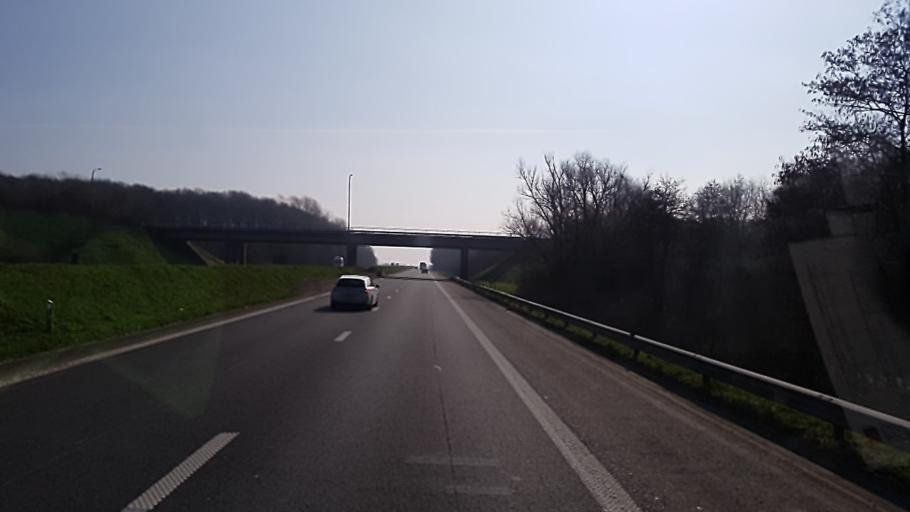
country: BE
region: Flanders
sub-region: Provincie West-Vlaanderen
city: Wervik
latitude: 50.8276
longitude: 3.0467
